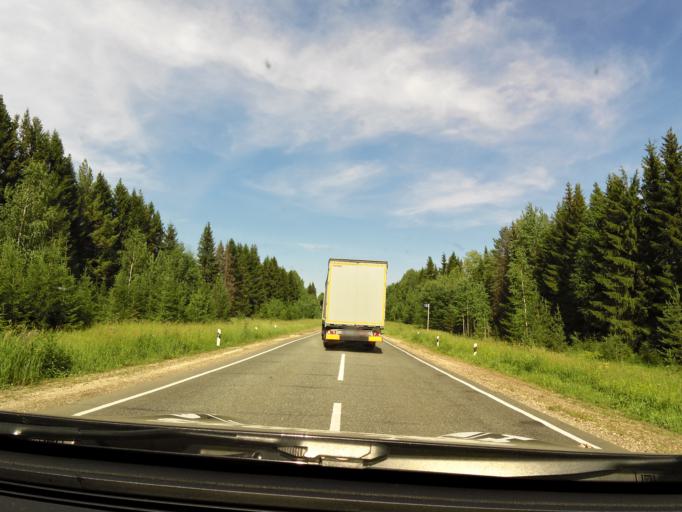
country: RU
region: Kirov
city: Belaya Kholunitsa
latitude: 58.8213
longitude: 50.6109
